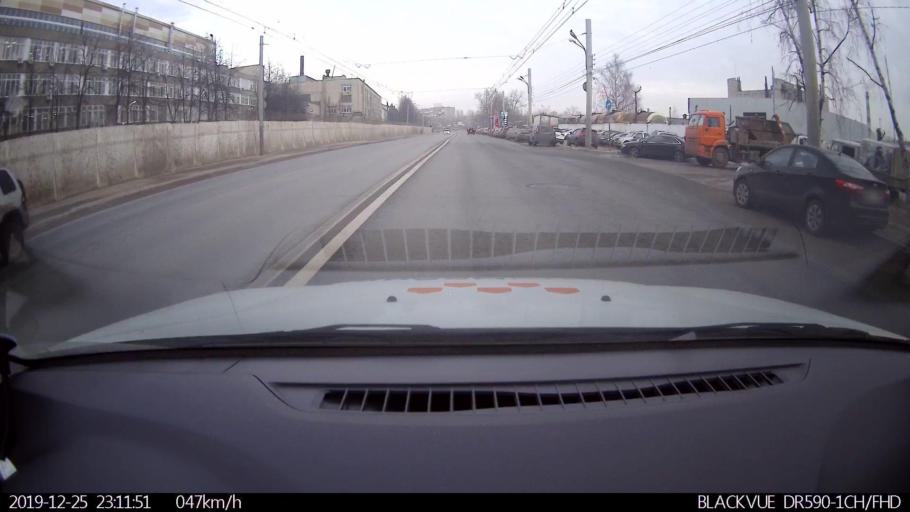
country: RU
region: Nizjnij Novgorod
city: Nizhniy Novgorod
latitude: 56.3211
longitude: 43.9082
